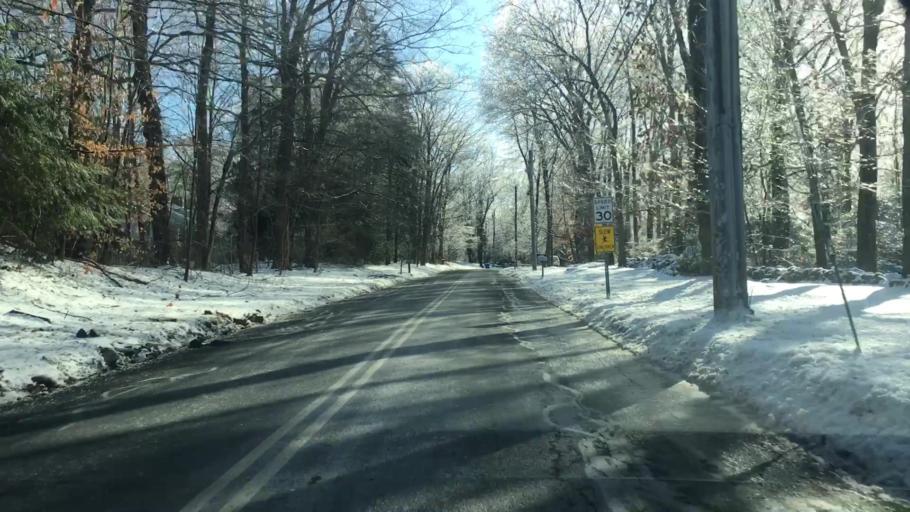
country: US
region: Connecticut
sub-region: Fairfield County
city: Trumbull
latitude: 41.3425
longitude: -73.2249
